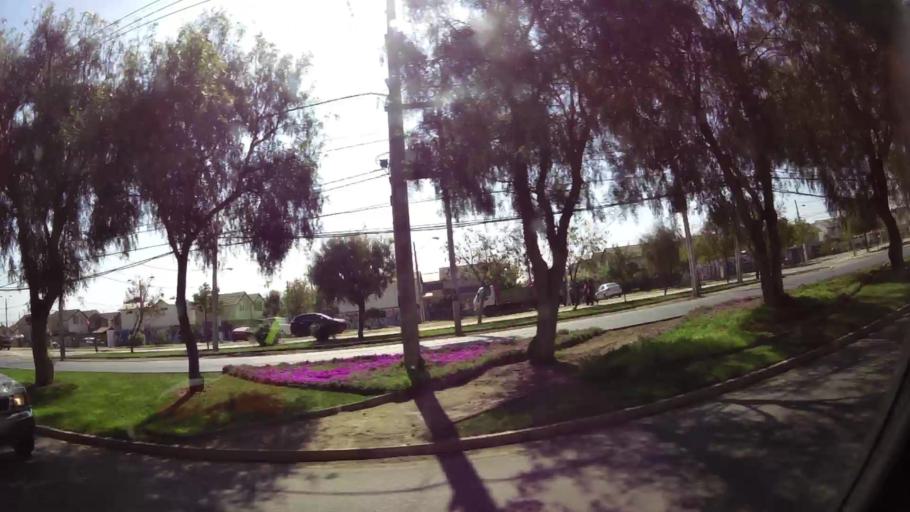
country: CL
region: Santiago Metropolitan
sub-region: Provincia de Santiago
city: Lo Prado
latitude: -33.5065
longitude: -70.7948
